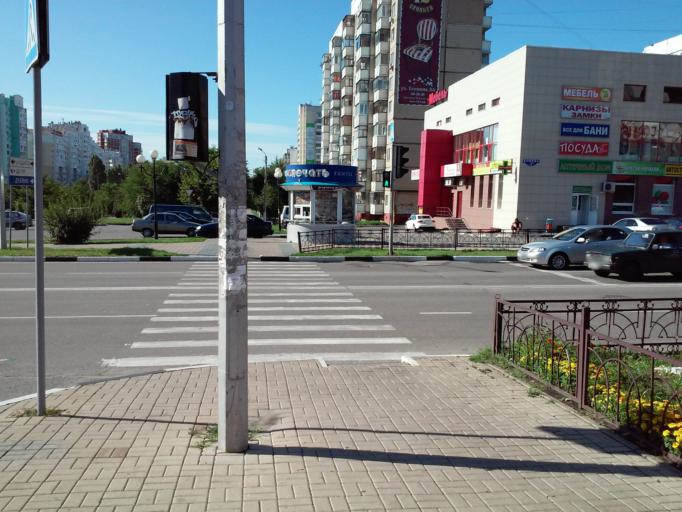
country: RU
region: Belgorod
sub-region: Belgorodskiy Rayon
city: Belgorod
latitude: 50.5604
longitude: 36.5709
